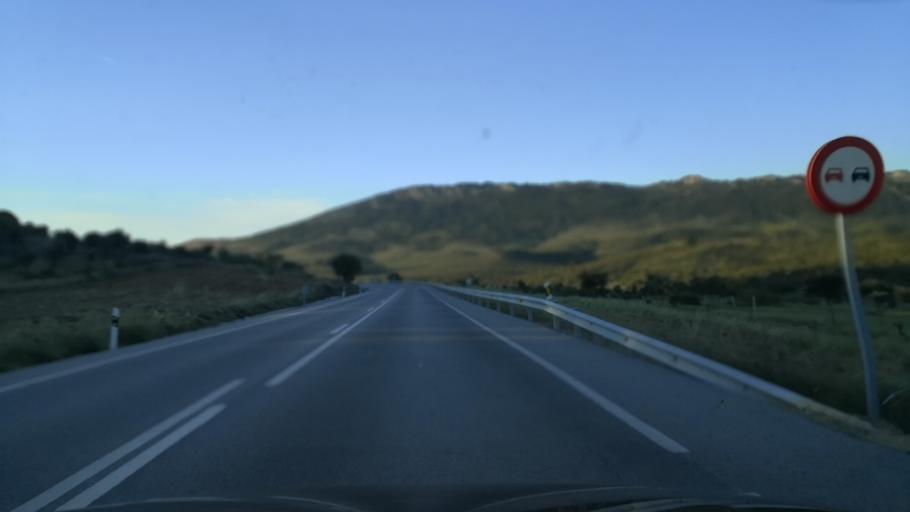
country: ES
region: Extremadura
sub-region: Provincia de Caceres
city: Valencia de Alcantara
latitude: 39.4595
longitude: -7.2039
